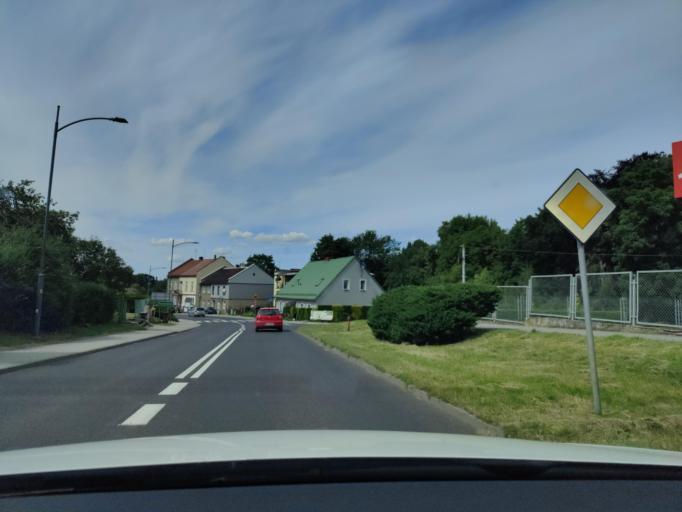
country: PL
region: Opole Voivodeship
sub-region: Powiat nyski
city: Glucholazy
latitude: 50.3106
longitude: 17.3902
